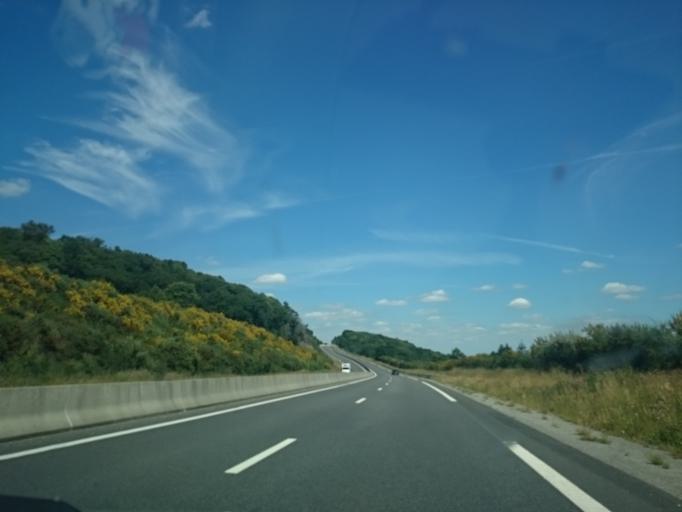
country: FR
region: Brittany
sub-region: Departement des Cotes-d'Armor
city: Mur-de-Bretagne
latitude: 48.2188
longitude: -3.0604
